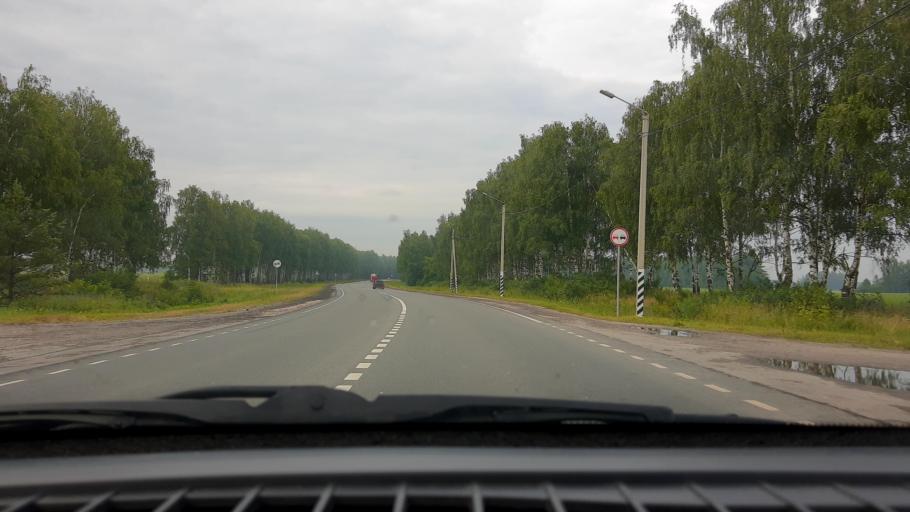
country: RU
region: Nizjnij Novgorod
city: Linda
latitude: 56.5641
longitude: 44.0243
